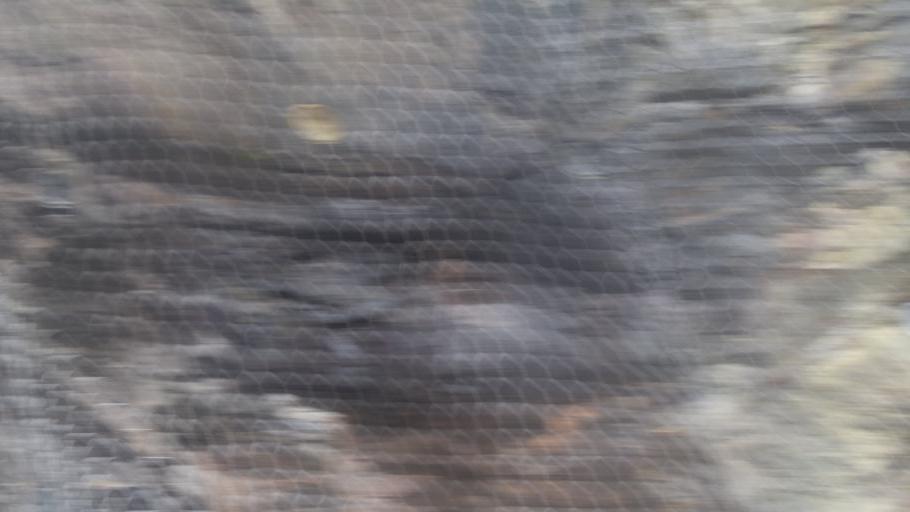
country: NO
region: Sor-Trondelag
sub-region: Selbu
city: Mebonden
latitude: 62.9642
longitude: 10.9694
